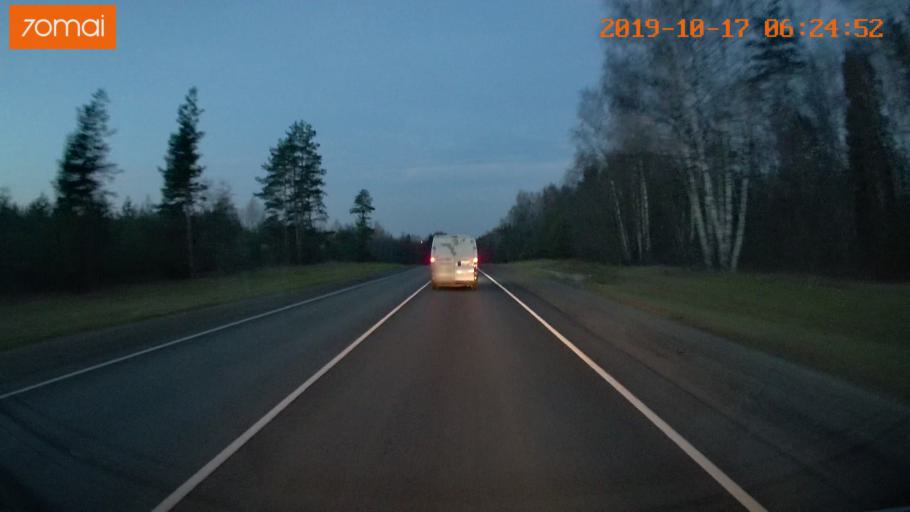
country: RU
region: Ivanovo
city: Lezhnevo
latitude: 56.7726
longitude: 40.8186
